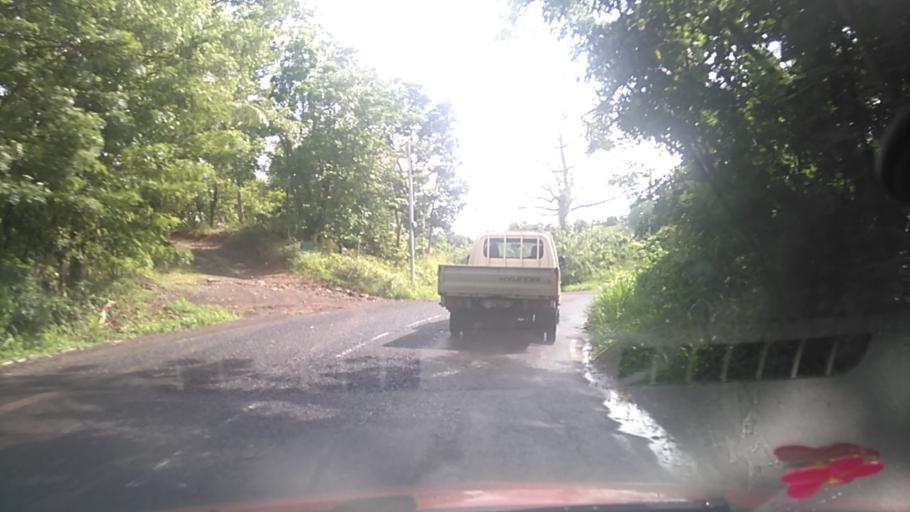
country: MQ
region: Martinique
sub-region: Martinique
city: Saint-Esprit
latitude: 14.5850
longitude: -60.9240
